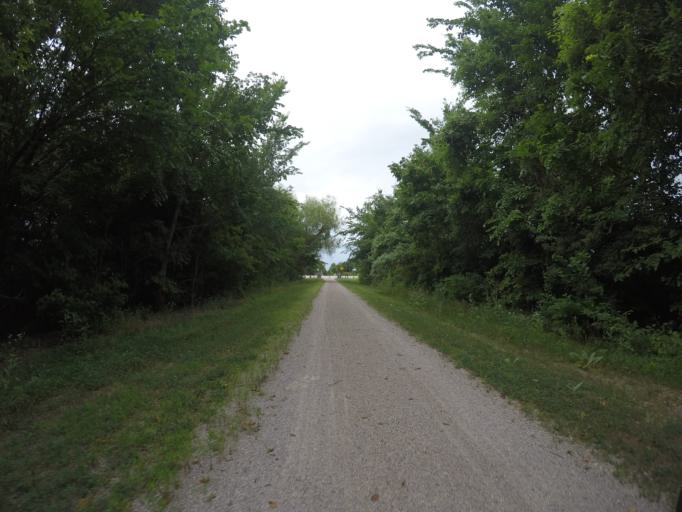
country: US
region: Kansas
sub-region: Franklin County
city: Ottawa
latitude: 38.5657
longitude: -95.2712
